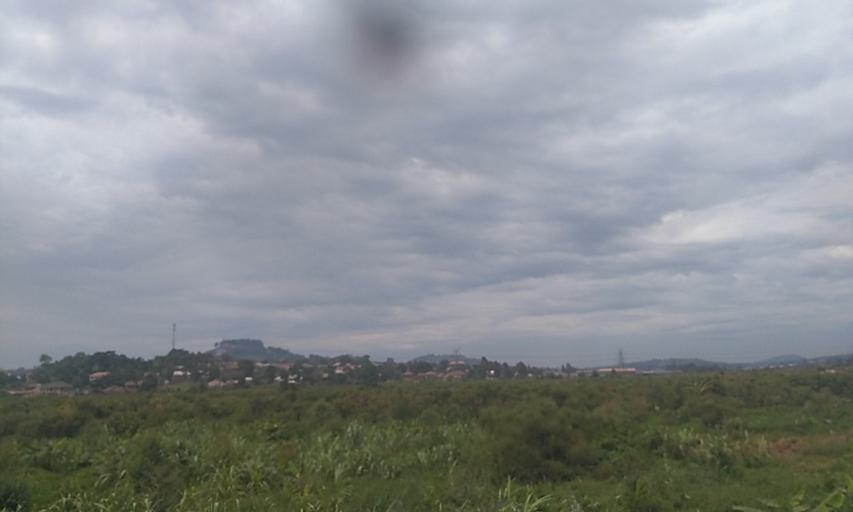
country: UG
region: Central Region
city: Kampala Central Division
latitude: 0.3303
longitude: 32.5257
